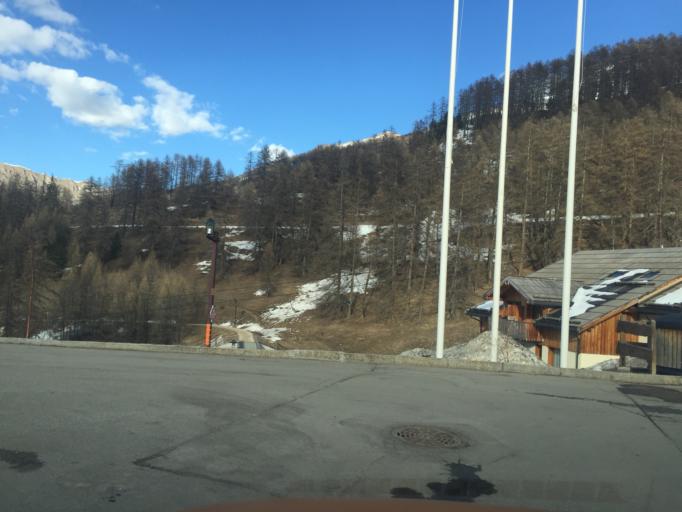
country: FR
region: Provence-Alpes-Cote d'Azur
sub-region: Departement des Hautes-Alpes
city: Embrun
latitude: 44.4857
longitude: 6.5540
